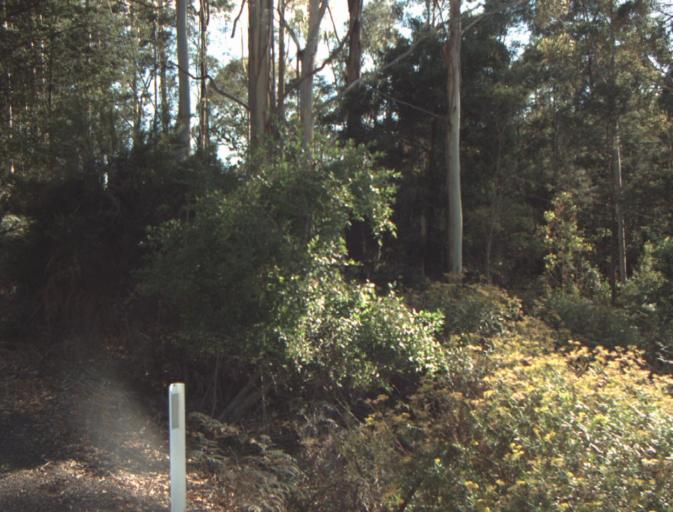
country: AU
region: Tasmania
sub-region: Launceston
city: Mayfield
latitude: -41.3017
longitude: 147.1986
